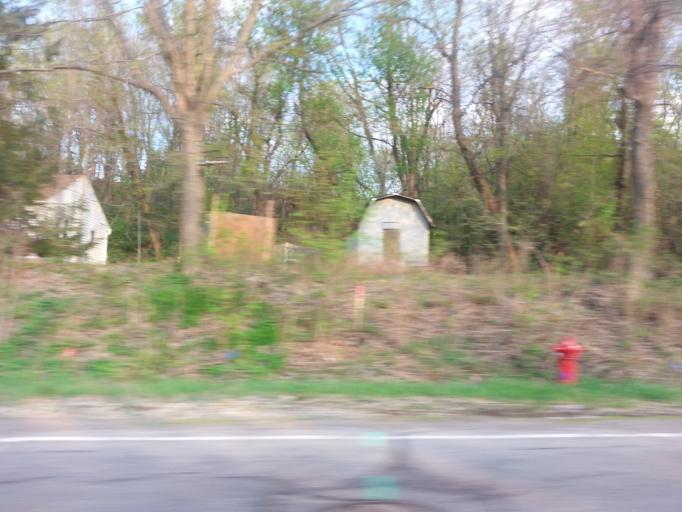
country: US
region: Minnesota
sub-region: Dakota County
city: Mendota Heights
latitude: 44.8929
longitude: -93.1516
